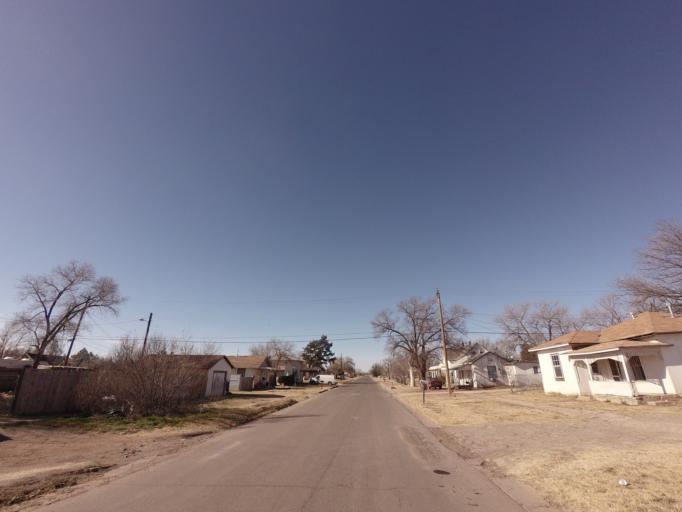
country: US
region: New Mexico
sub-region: Curry County
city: Clovis
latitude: 34.4018
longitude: -103.2095
